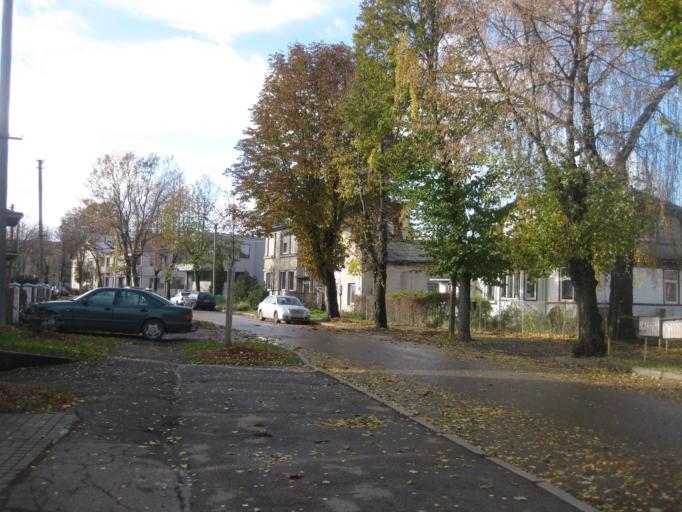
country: LT
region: Kauno apskritis
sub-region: Kaunas
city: Eiguliai
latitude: 54.9043
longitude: 23.9391
